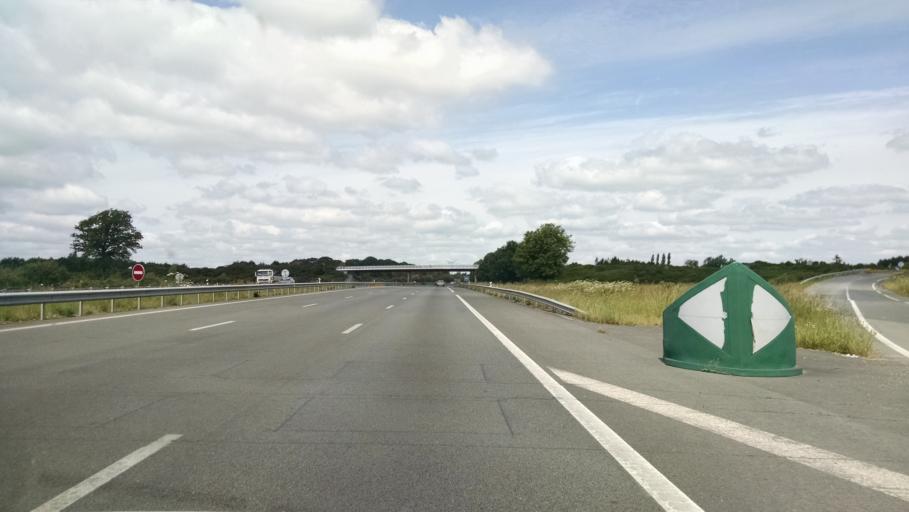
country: FR
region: Pays de la Loire
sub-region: Departement de la Loire-Atlantique
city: Malville
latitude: 47.3547
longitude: -1.8884
